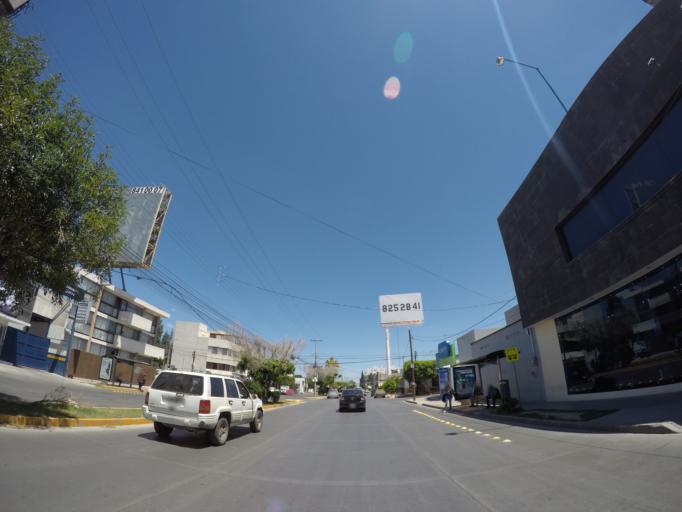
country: MX
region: San Luis Potosi
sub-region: San Luis Potosi
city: San Luis Potosi
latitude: 22.1444
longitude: -101.0043
